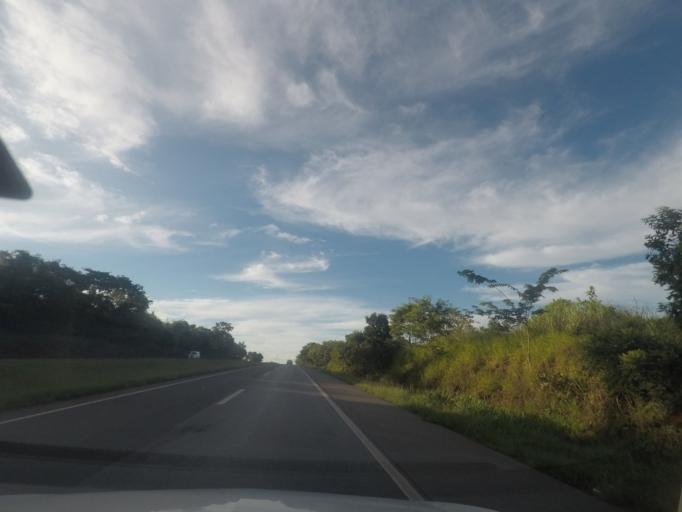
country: BR
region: Goias
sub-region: Itumbiara
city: Itumbiara
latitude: -18.2281
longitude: -49.2637
